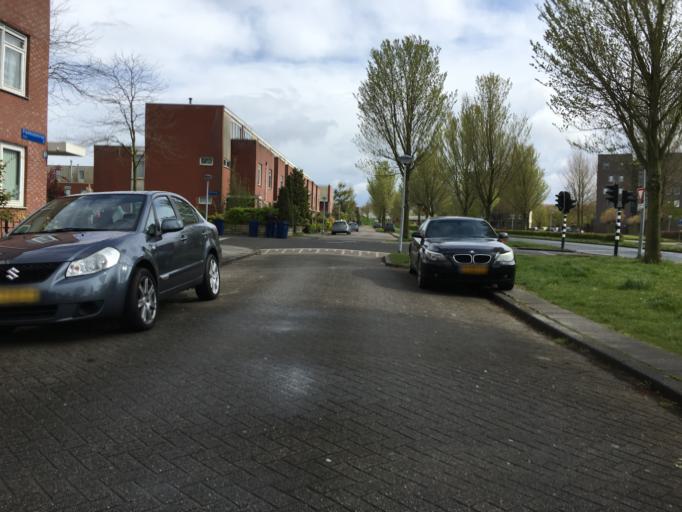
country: NL
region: Flevoland
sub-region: Gemeente Almere
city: Almere Stad
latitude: 52.3706
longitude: 5.2516
